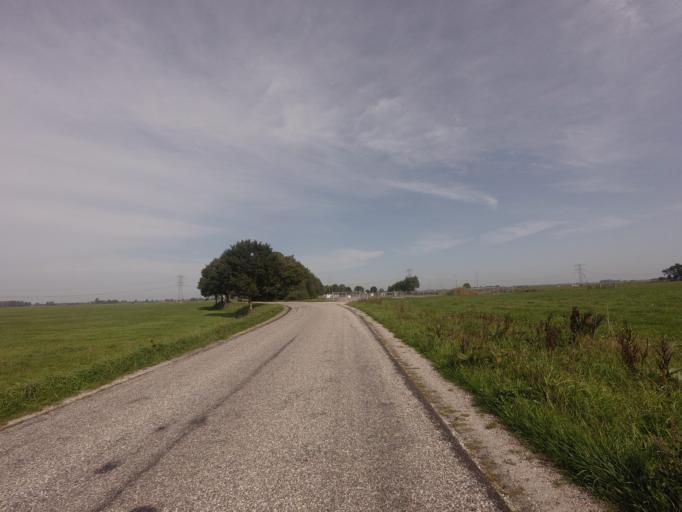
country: NL
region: Groningen
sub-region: Gemeente Leek
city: Leek
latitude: 53.1919
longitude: 6.3556
